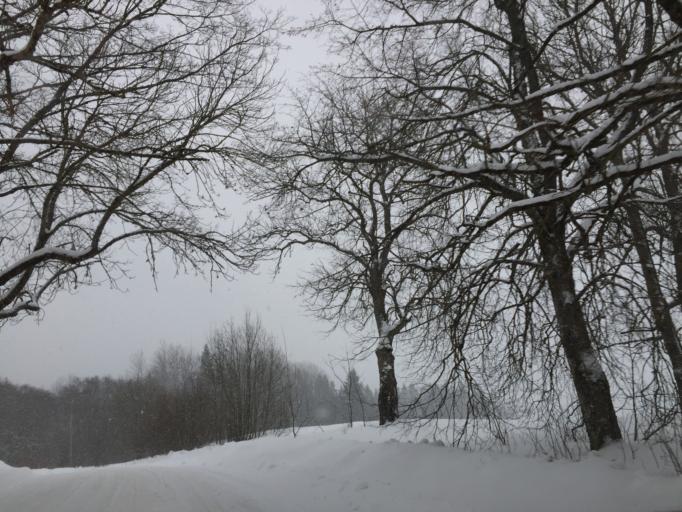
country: LV
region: Amatas Novads
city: Drabesi
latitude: 57.0690
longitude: 25.3305
